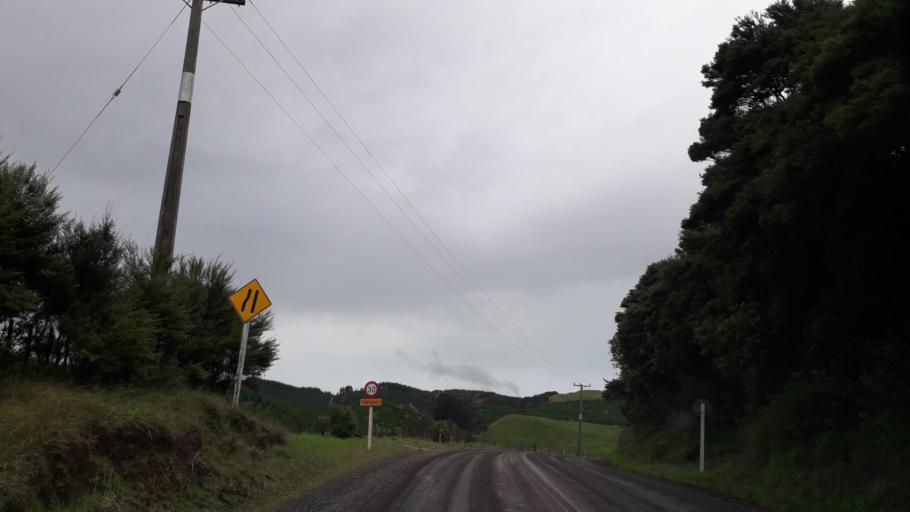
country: NZ
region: Northland
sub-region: Far North District
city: Ahipara
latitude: -35.4326
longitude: 173.3472
